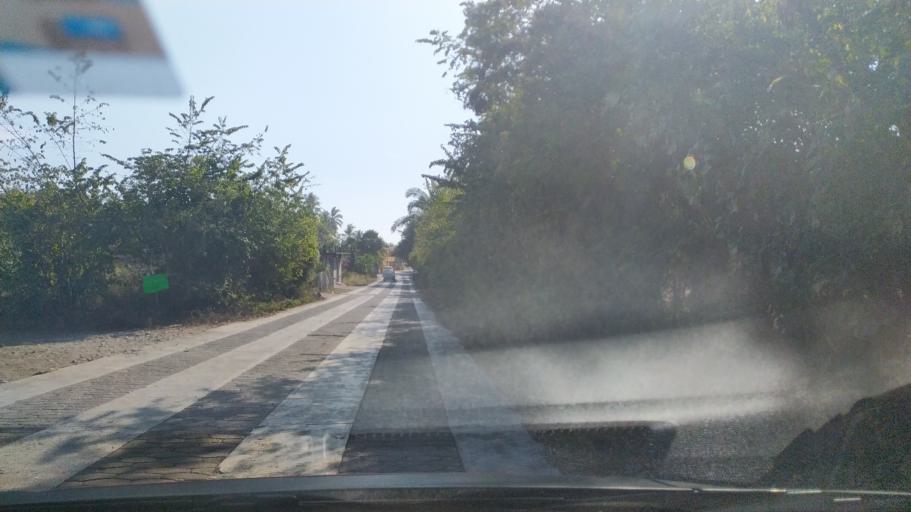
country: MX
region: Michoacan
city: Coahuayana Viejo
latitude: 18.5851
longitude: -103.6732
